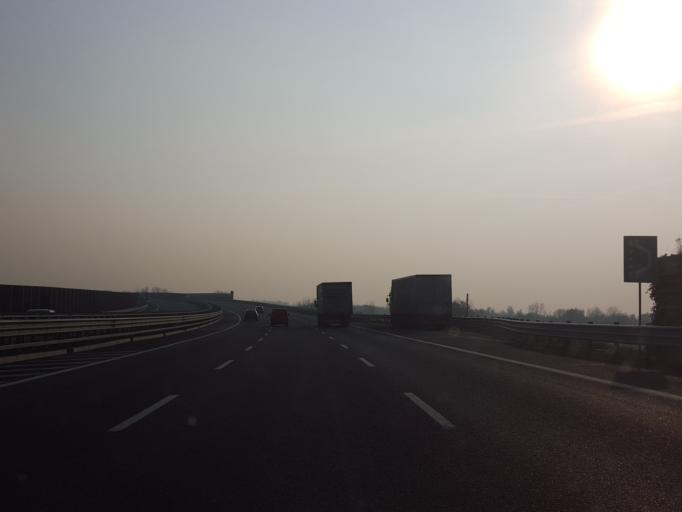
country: IT
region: Veneto
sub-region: Provincia di Venezia
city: Maerne
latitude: 45.5266
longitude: 12.1398
